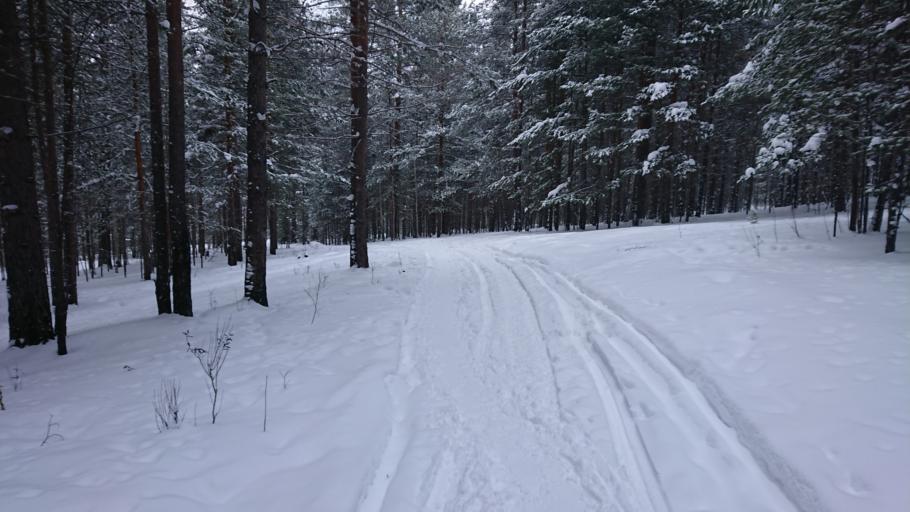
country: RU
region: Sverdlovsk
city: Degtyarsk
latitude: 56.6950
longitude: 60.0656
